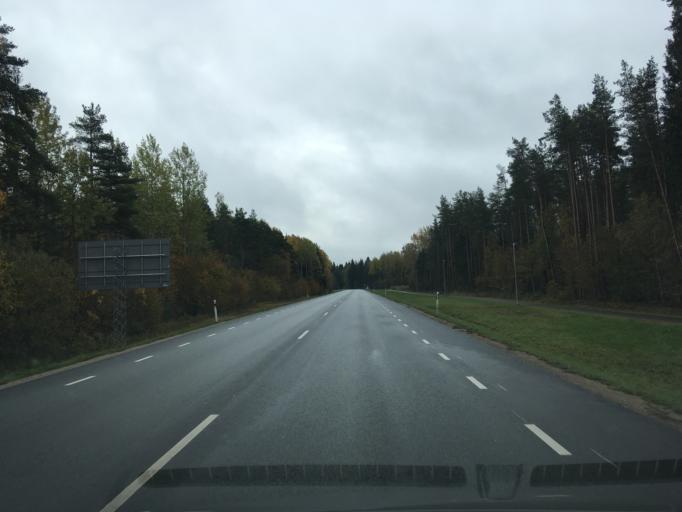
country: EE
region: Harju
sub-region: Saku vald
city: Saku
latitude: 59.3063
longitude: 24.6350
